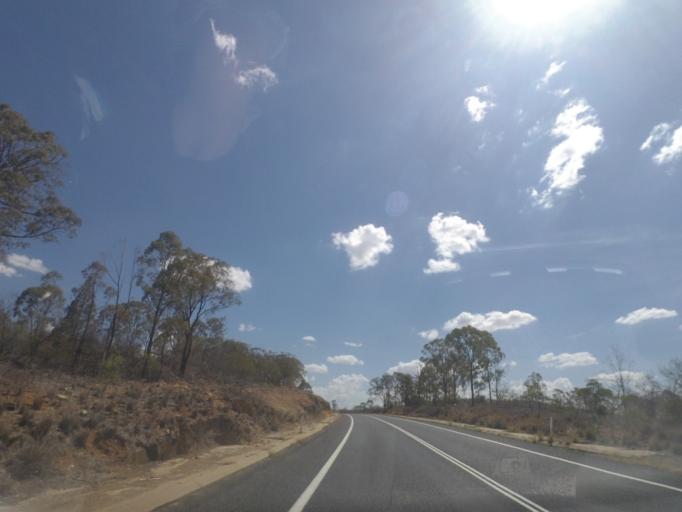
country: AU
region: Queensland
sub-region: Southern Downs
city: Warwick
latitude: -28.2192
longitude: 151.5572
